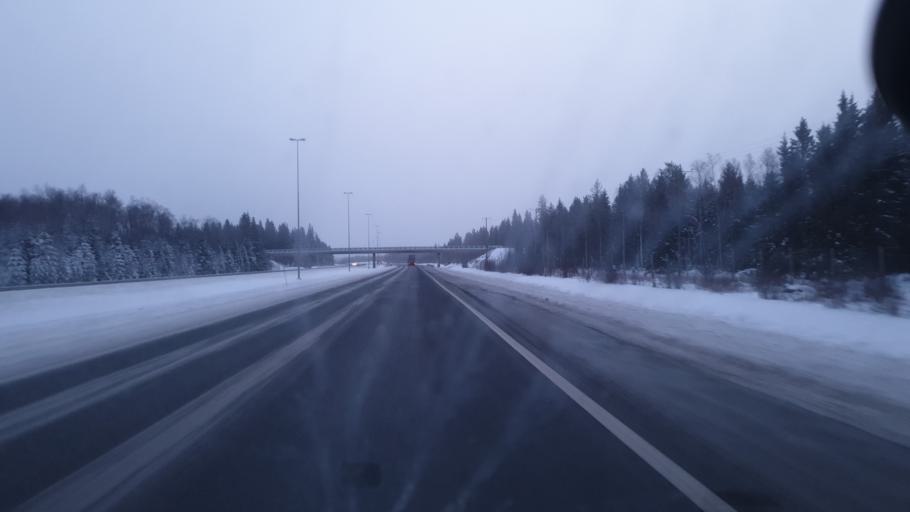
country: FI
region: Lapland
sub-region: Kemi-Tornio
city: Keminmaa
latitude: 65.8295
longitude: 24.3709
